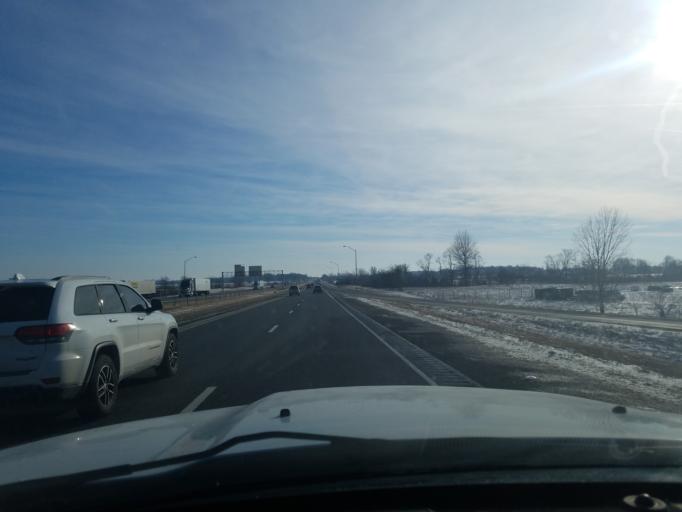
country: US
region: Indiana
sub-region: Madison County
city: Alexandria
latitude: 40.2752
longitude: -85.5581
